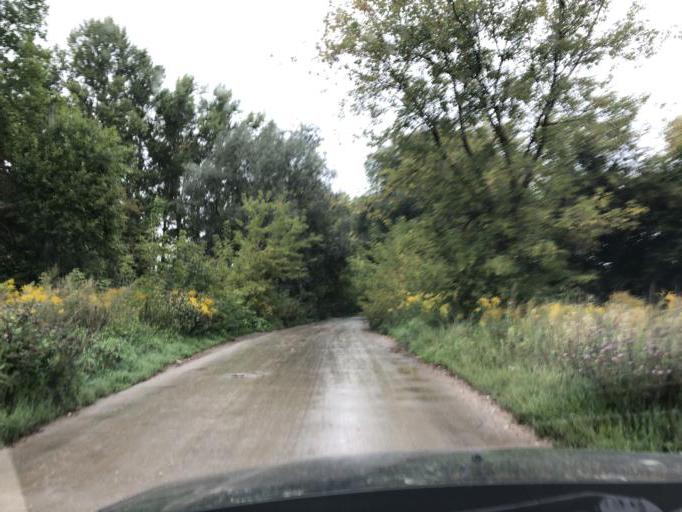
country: RU
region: Tula
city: Mendeleyevskiy
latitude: 54.1722
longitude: 37.5529
